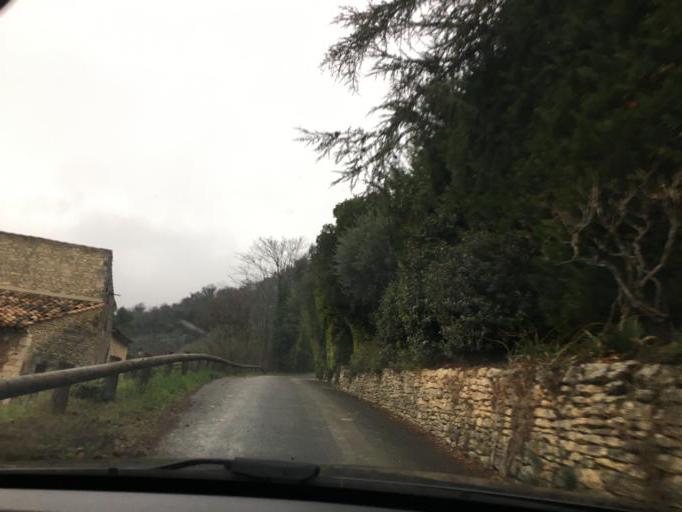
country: FR
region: Provence-Alpes-Cote d'Azur
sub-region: Departement du Vaucluse
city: Gordes
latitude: 43.9109
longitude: 5.2053
